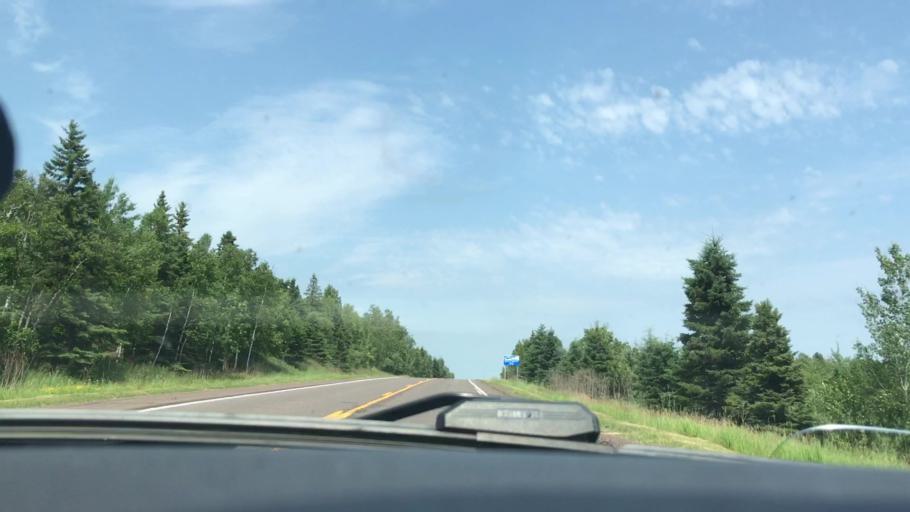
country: US
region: Minnesota
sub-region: Lake County
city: Silver Bay
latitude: 47.4468
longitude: -91.0653
